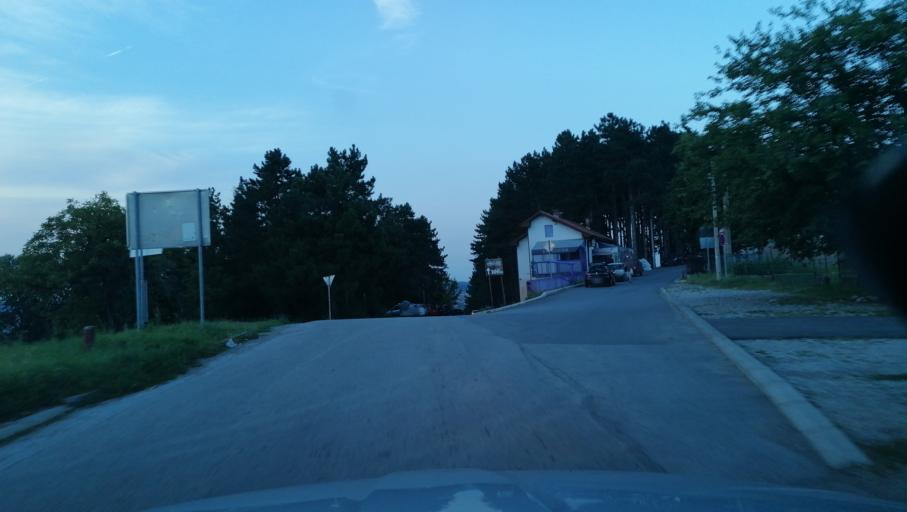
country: RS
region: Central Serbia
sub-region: Kolubarski Okrug
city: Valjevo
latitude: 44.2598
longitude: 19.8777
